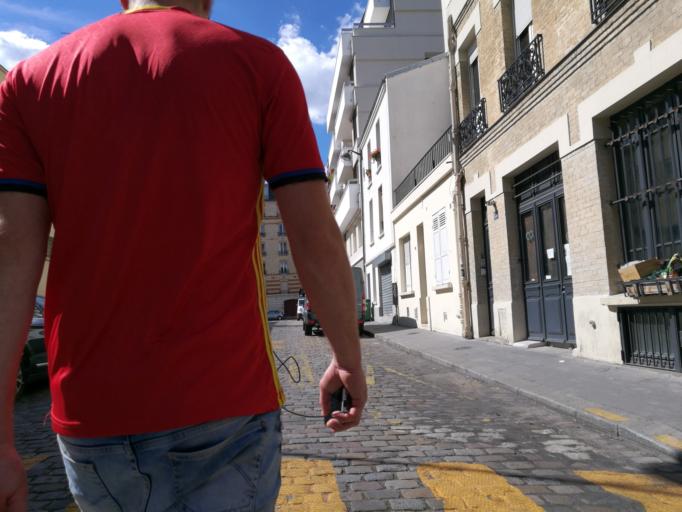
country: FR
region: Ile-de-France
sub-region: Paris
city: Saint-Ouen
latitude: 48.8967
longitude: 2.3431
